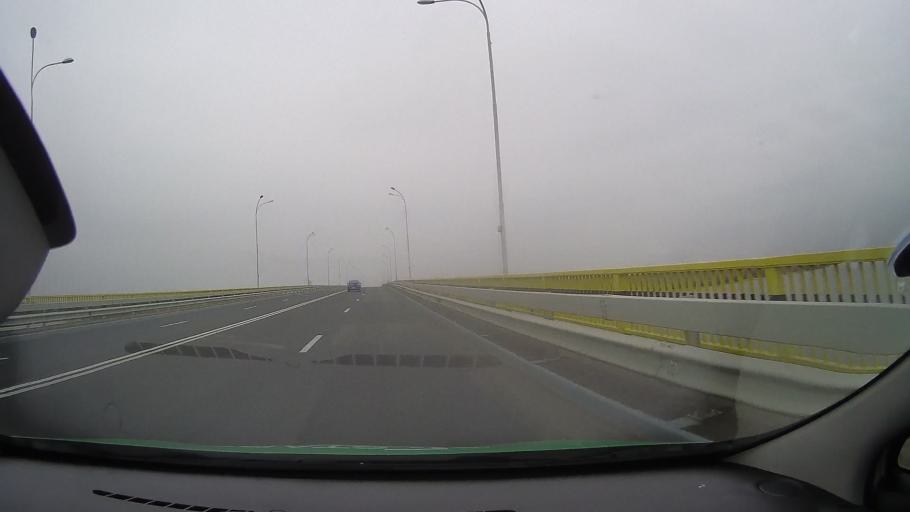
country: RO
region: Ialomita
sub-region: Comuna Giurgeni
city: Giurgeni
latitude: 44.7540
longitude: 27.8801
